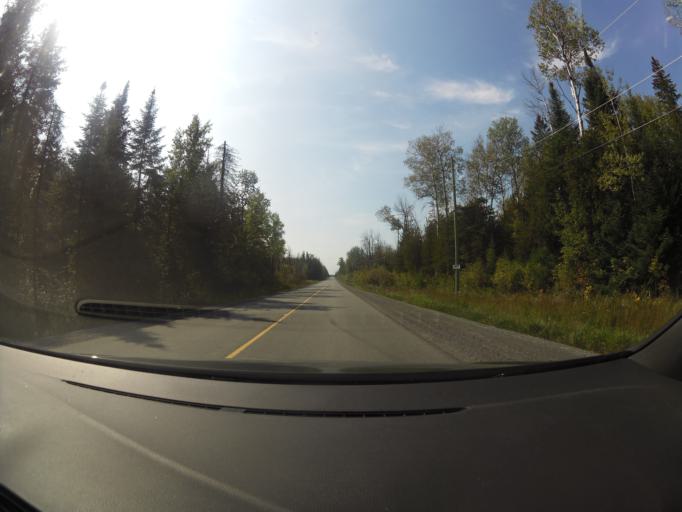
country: CA
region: Ontario
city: Carleton Place
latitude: 45.3293
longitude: -76.1678
